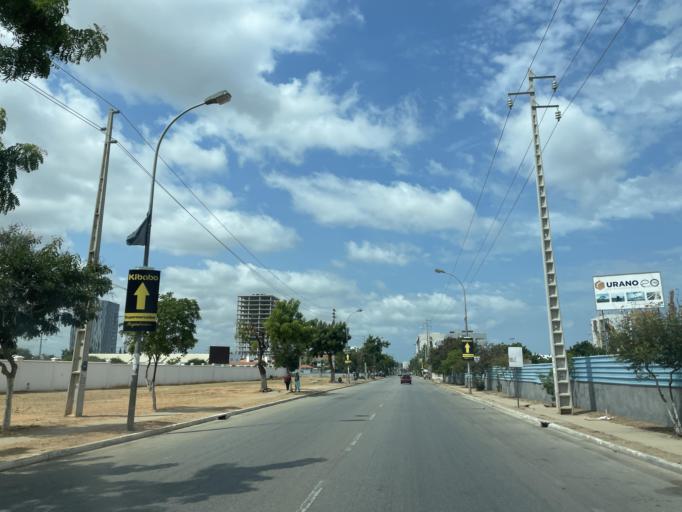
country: AO
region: Luanda
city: Luanda
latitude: -8.9166
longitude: 13.1900
